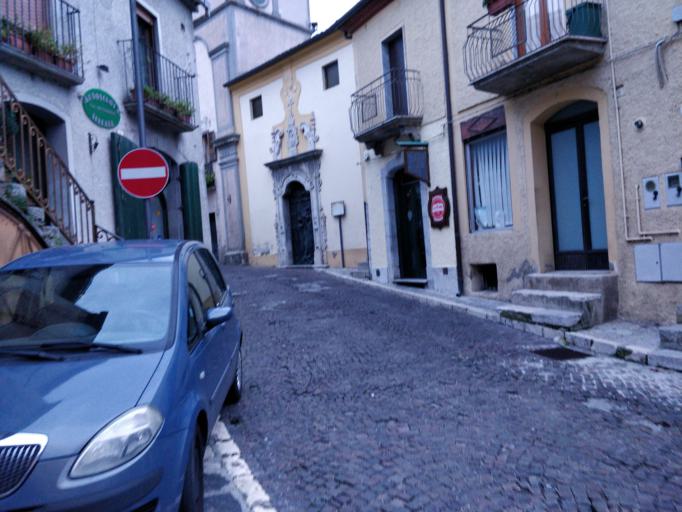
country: IT
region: Basilicate
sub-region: Provincia di Potenza
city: Pignola
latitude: 40.5738
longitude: 15.7875
